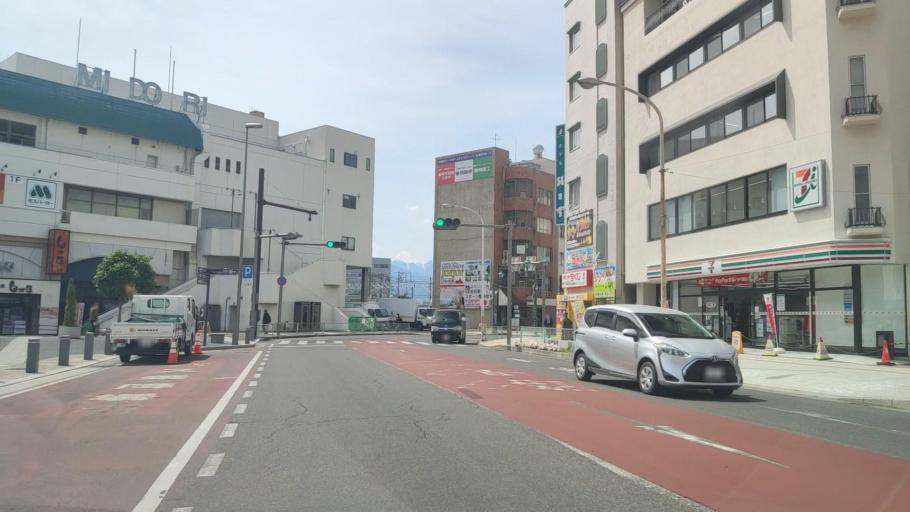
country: JP
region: Nagano
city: Matsumoto
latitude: 36.2314
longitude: 137.9653
